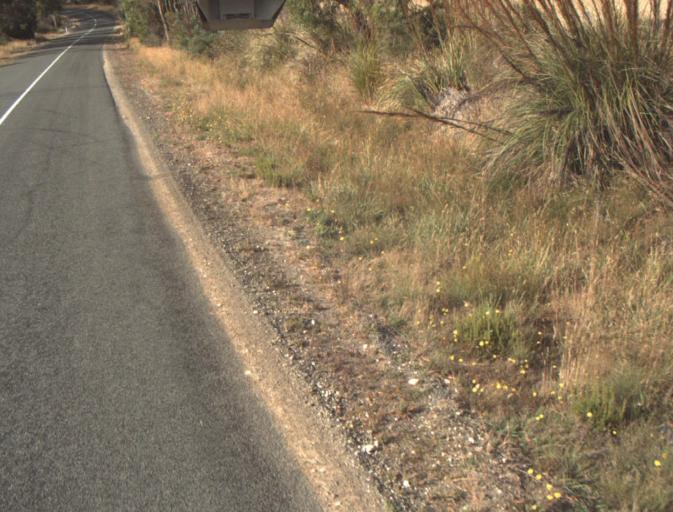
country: AU
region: Tasmania
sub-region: Dorset
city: Bridport
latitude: -41.1109
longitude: 147.2006
